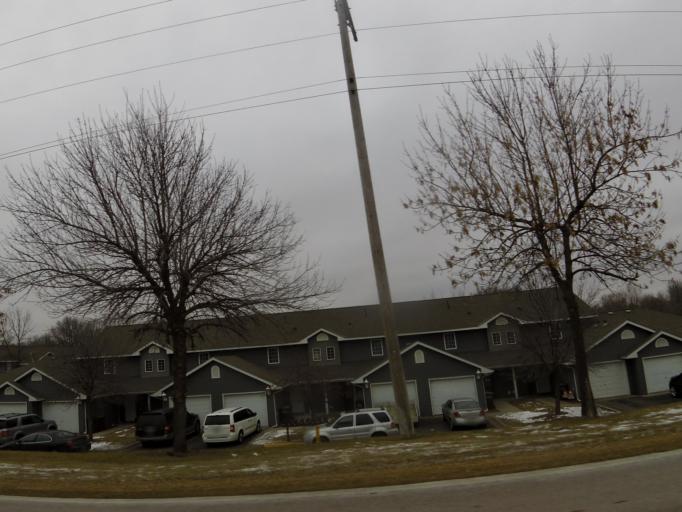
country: US
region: Minnesota
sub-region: Carver County
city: Watertown
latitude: 44.9587
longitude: -93.8377
